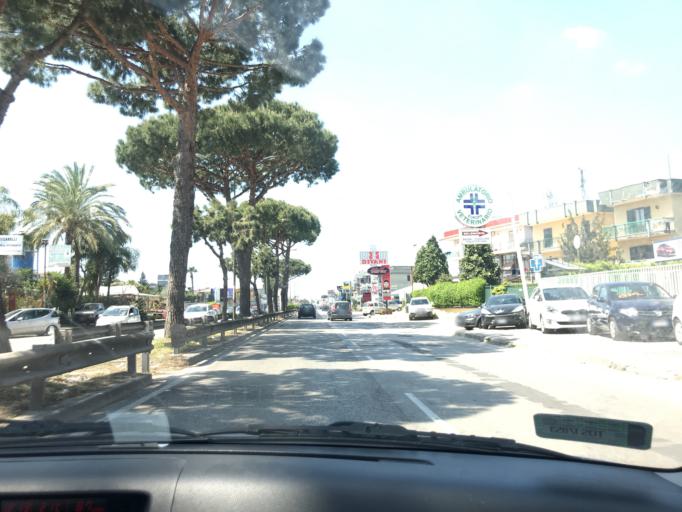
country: IT
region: Campania
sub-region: Provincia di Napoli
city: Villaricca
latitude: 40.9205
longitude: 14.1794
